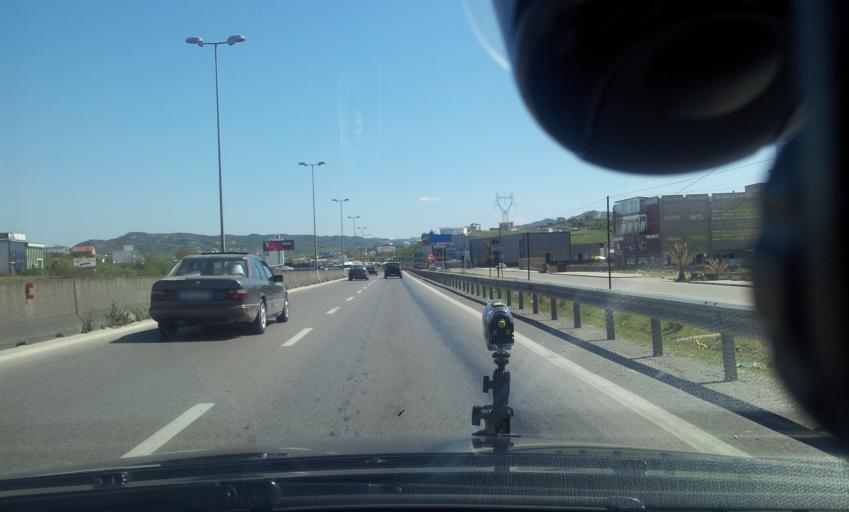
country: AL
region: Tirane
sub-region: Rrethi i Tiranes
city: Berxull
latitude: 41.3780
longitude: 19.6742
